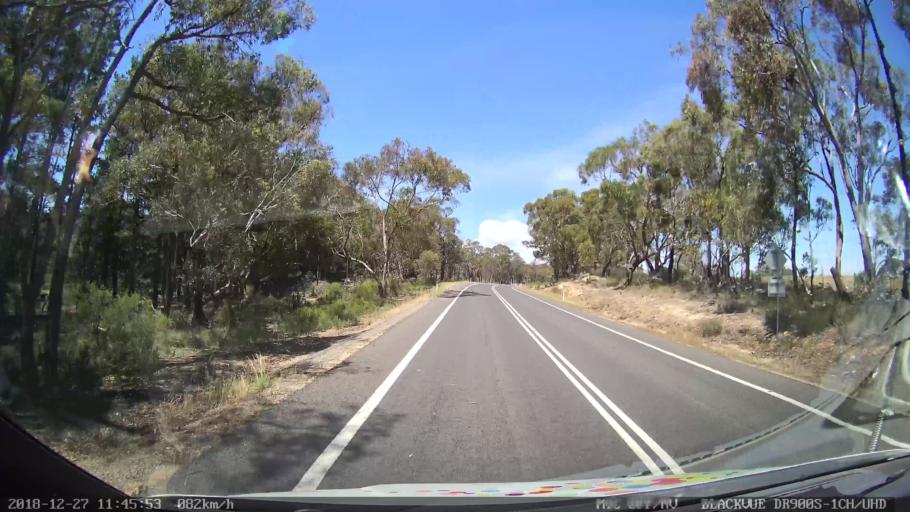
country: AU
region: New South Wales
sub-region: Bathurst Regional
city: Perthville
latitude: -33.5856
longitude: 149.4646
